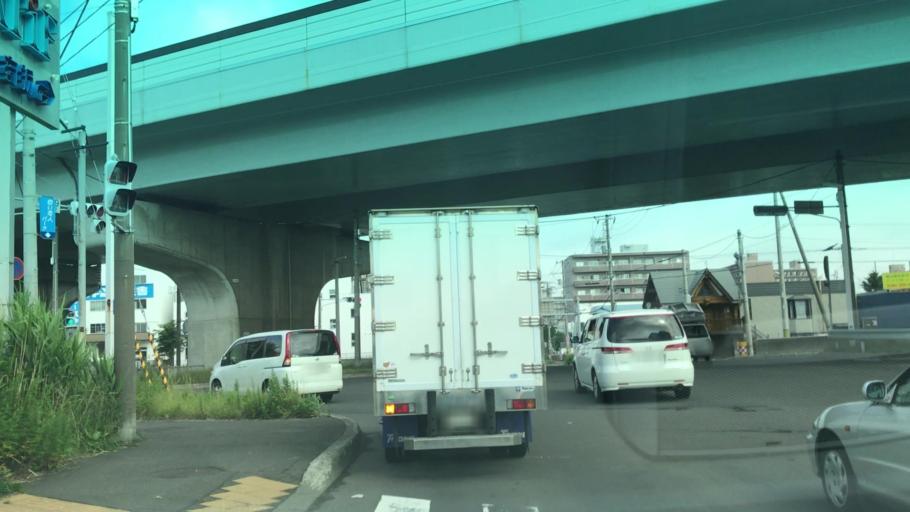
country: JP
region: Hokkaido
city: Sapporo
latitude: 43.0929
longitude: 141.2846
